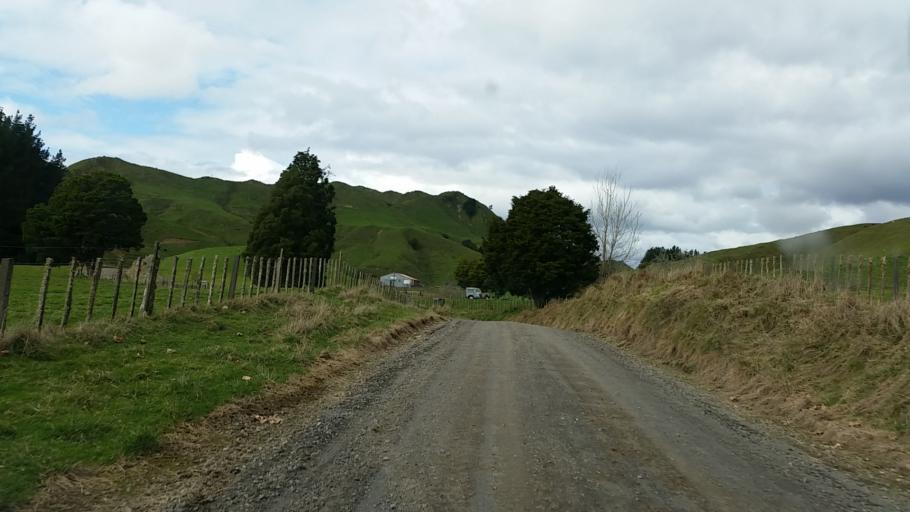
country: NZ
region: Taranaki
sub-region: New Plymouth District
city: Waitara
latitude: -39.1608
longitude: 174.5916
